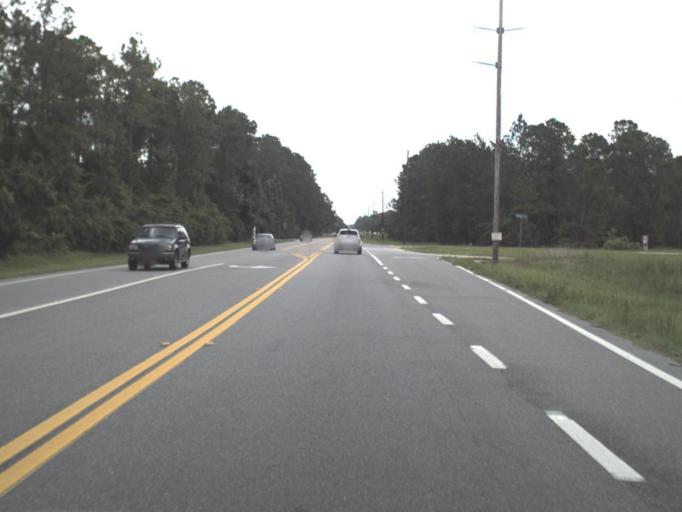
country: US
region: Florida
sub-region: Putnam County
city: Palatka
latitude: 29.5836
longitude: -81.6139
